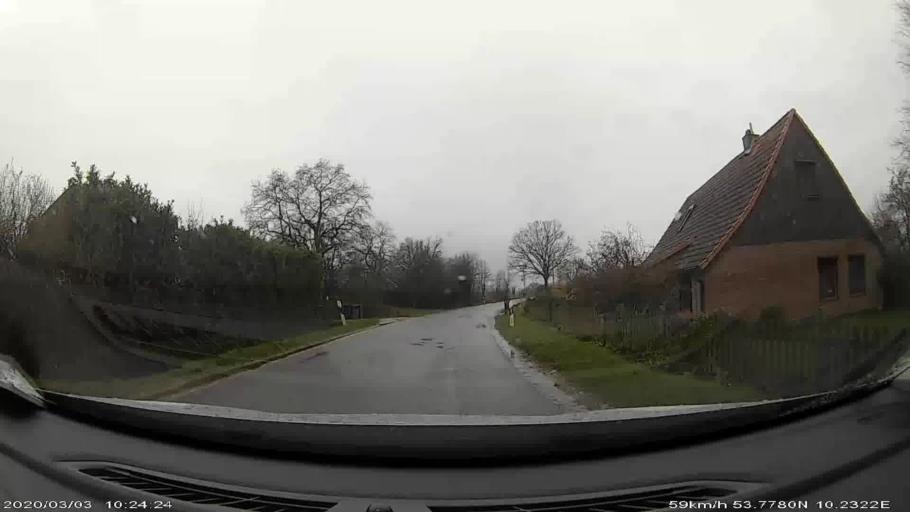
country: DE
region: Schleswig-Holstein
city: Sulfeld
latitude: 53.7782
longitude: 10.2274
